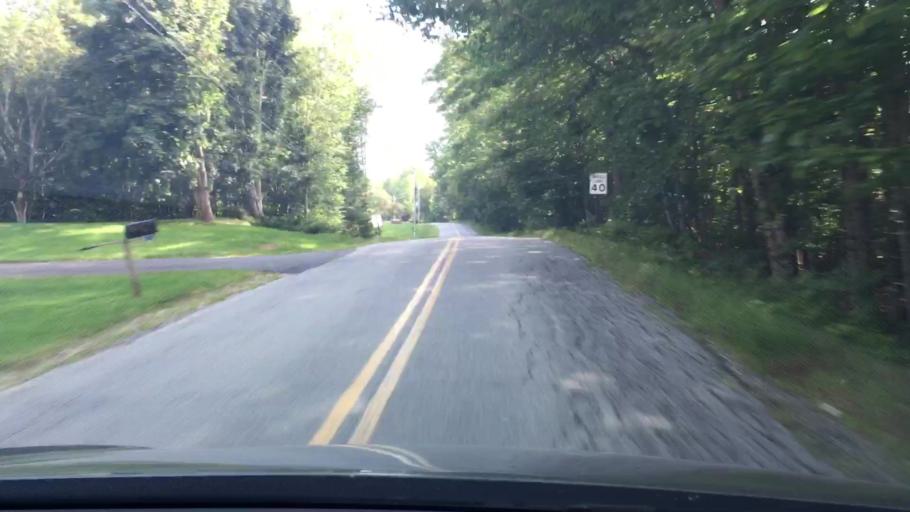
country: US
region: Maine
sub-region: Hancock County
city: Bucksport
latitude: 44.5516
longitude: -68.7965
